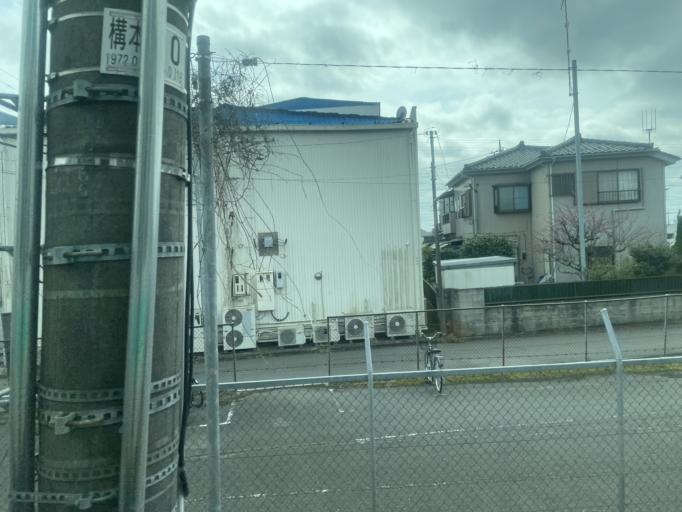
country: JP
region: Ibaraki
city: Ryugasaki
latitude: 35.8352
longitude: 140.2436
